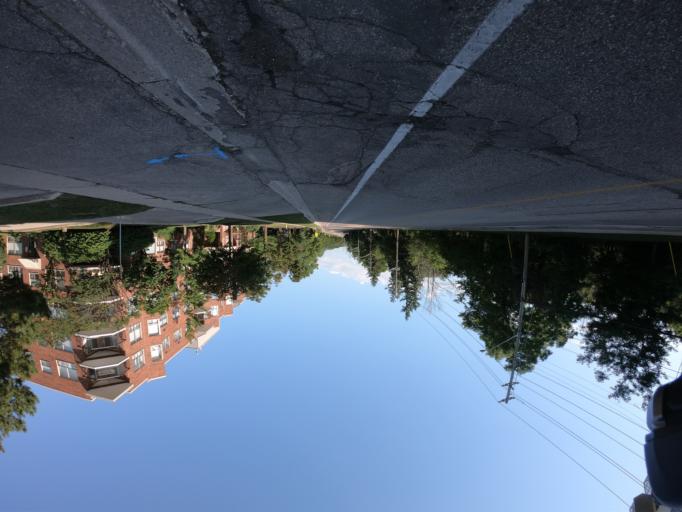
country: CA
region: Ontario
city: Waterloo
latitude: 43.4623
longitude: -80.5437
